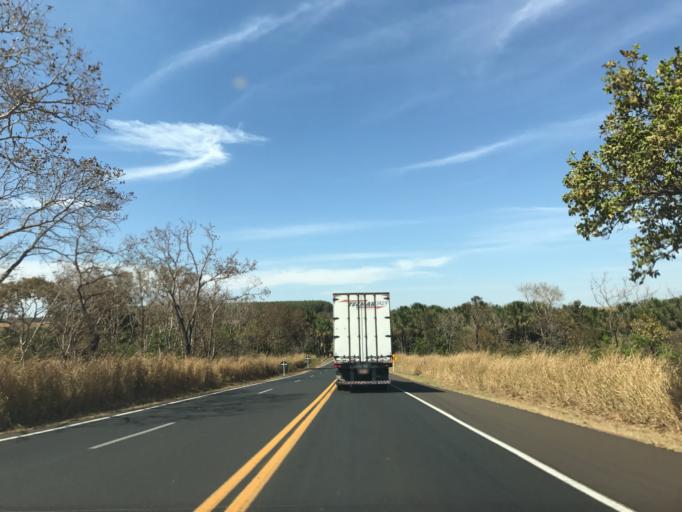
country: BR
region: Minas Gerais
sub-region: Monte Alegre De Minas
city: Monte Alegre de Minas
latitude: -18.9904
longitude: -49.0215
